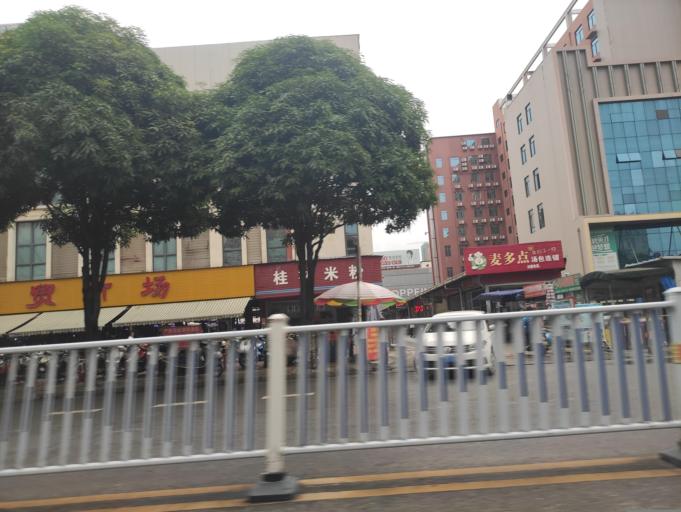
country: CN
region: Guangxi Zhuangzu Zizhiqu
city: Baise City
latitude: 23.8907
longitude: 106.6302
